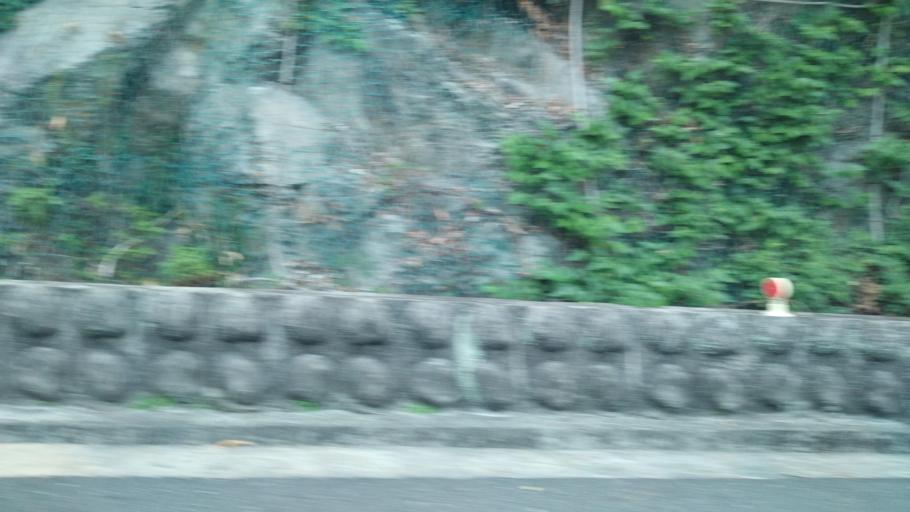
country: TW
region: Taiwan
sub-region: Hualien
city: Hualian
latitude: 24.2220
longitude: 121.6977
